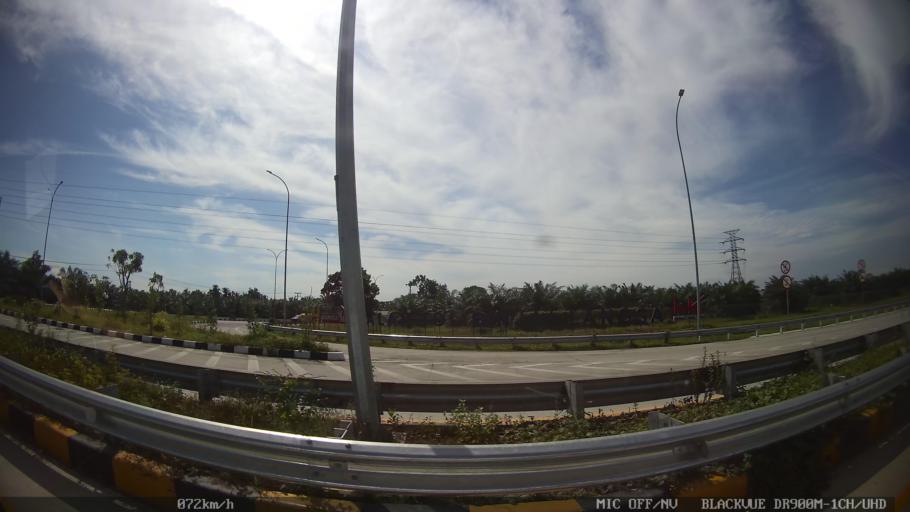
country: ID
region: North Sumatra
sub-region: Kabupaten Langkat
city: Stabat
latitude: 3.7309
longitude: 98.4902
